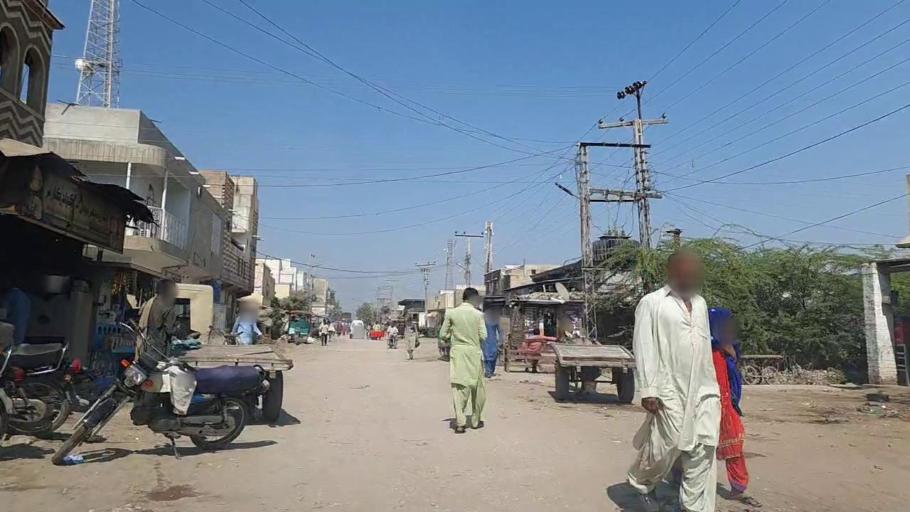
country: PK
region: Sindh
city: Naukot
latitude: 24.8577
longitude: 69.4037
